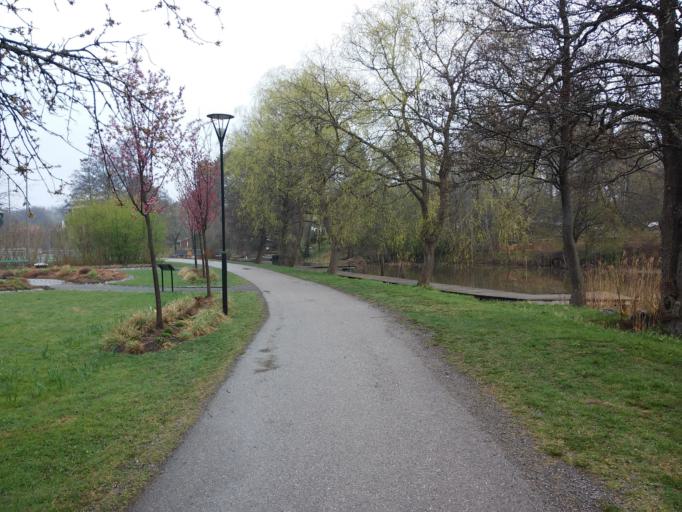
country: SE
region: Stockholm
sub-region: Osterakers Kommun
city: Akersberga
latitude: 59.4854
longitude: 18.2885
